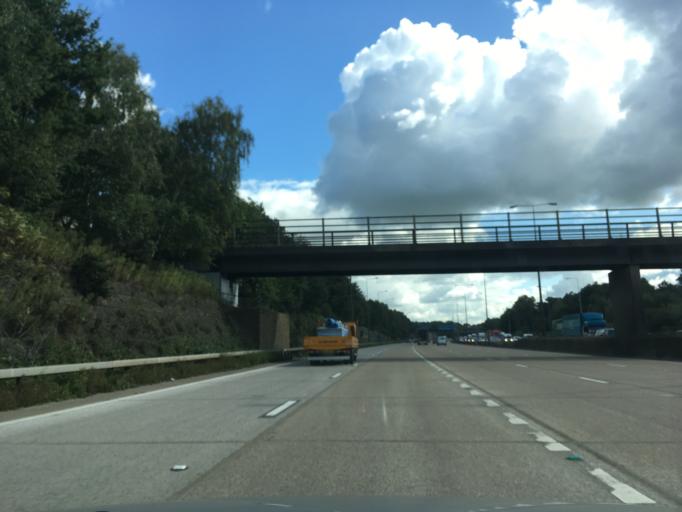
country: GB
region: England
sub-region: Surrey
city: Byfleet
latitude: 51.3245
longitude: -0.4605
